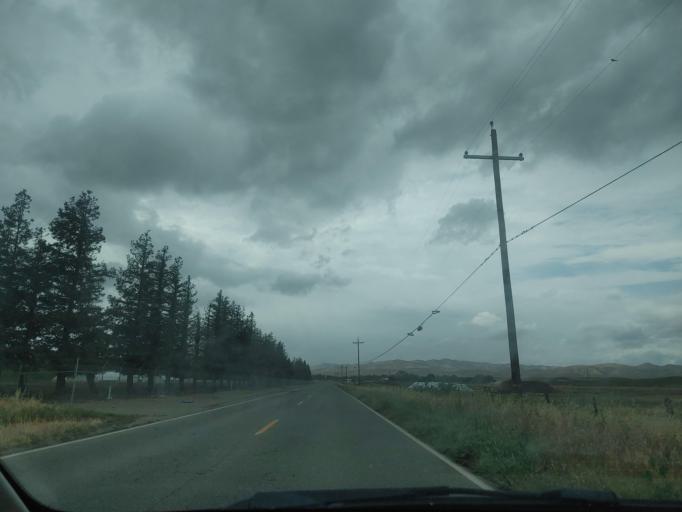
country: US
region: California
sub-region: Stanislaus County
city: Newman
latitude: 37.3324
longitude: -121.0917
